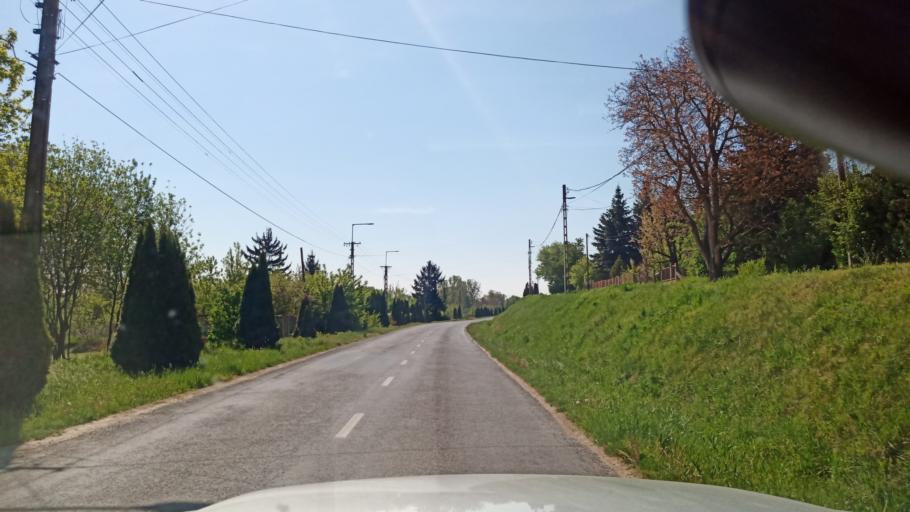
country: HU
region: Zala
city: Sarmellek
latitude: 46.7591
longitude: 17.1069
